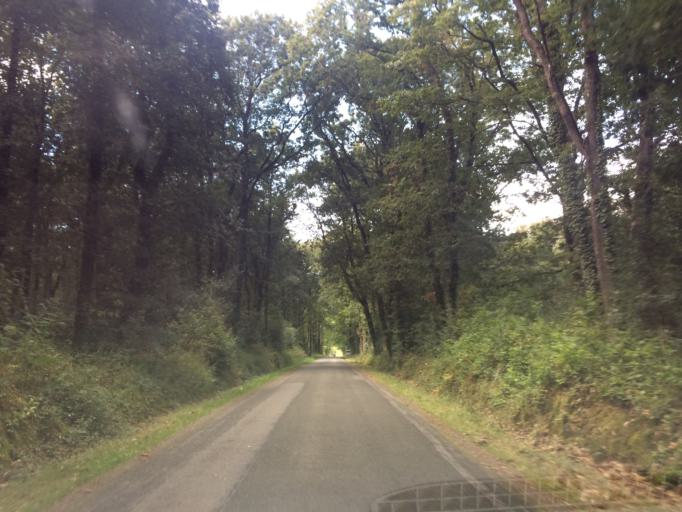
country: FR
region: Pays de la Loire
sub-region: Departement de la Loire-Atlantique
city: Rouans
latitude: 47.1528
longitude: -1.8908
